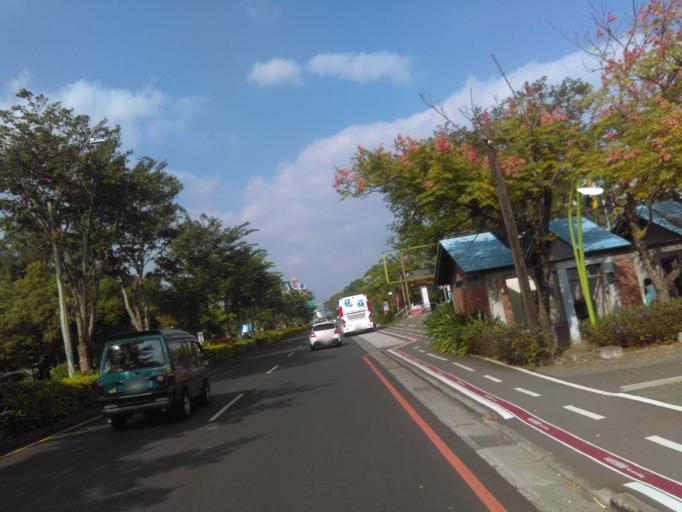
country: TW
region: Taiwan
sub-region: Yilan
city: Yilan
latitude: 24.7524
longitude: 121.7567
